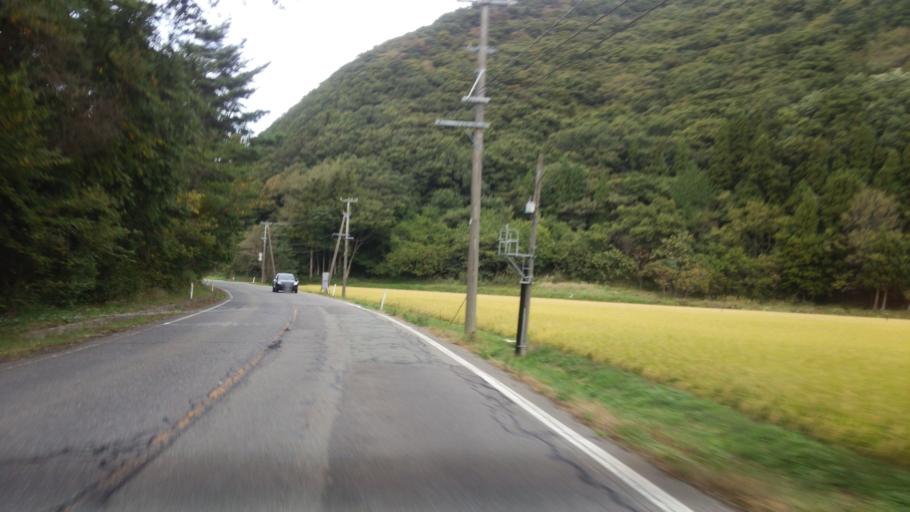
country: JP
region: Fukushima
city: Inawashiro
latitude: 37.4706
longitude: 140.1526
